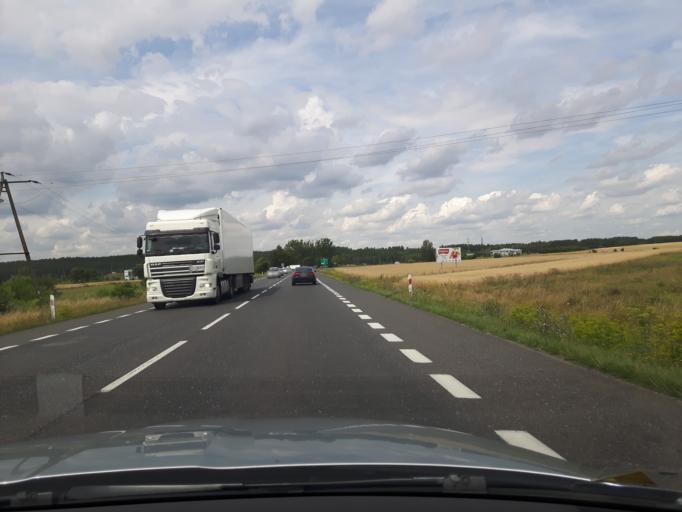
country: PL
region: Masovian Voivodeship
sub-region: Powiat mlawski
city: Mlawa
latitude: 53.1230
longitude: 20.3947
